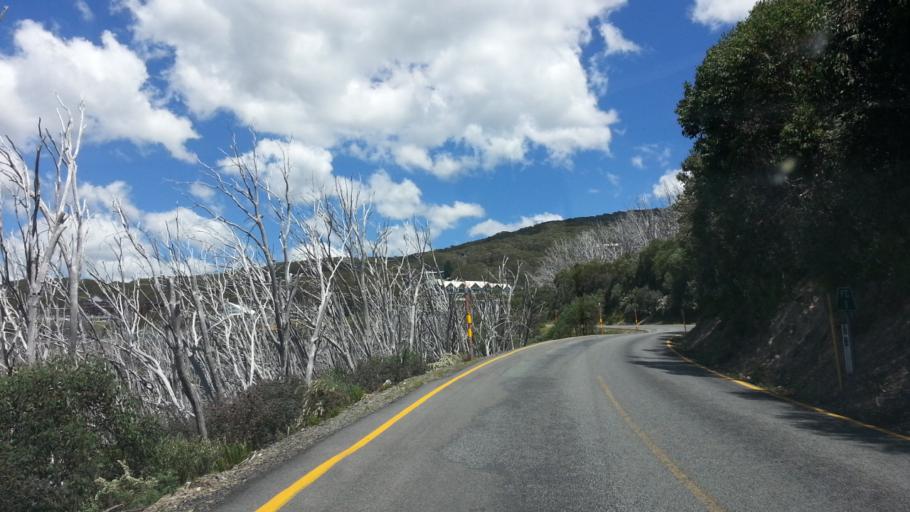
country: AU
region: Victoria
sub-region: Alpine
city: Mount Beauty
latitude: -36.8587
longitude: 147.2755
